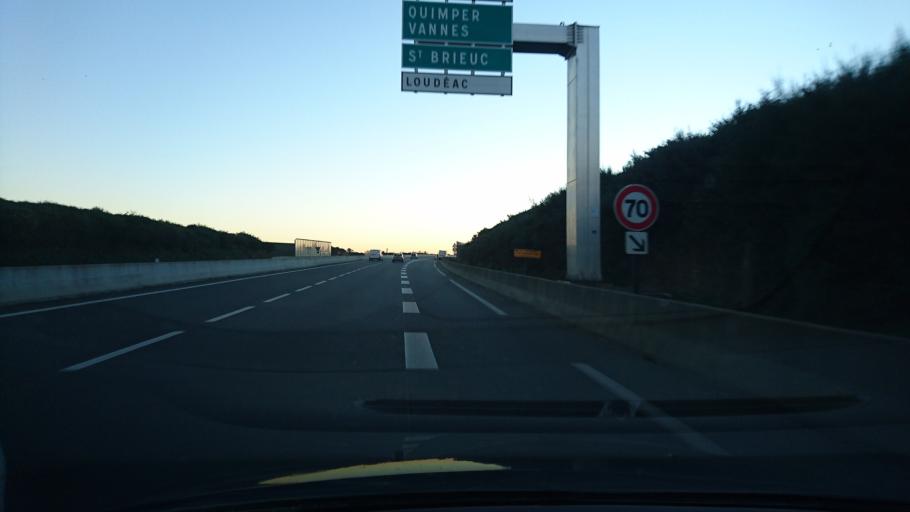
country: FR
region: Brittany
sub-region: Departement des Cotes-d'Armor
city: Ploufragan
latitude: 48.4786
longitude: -2.7731
